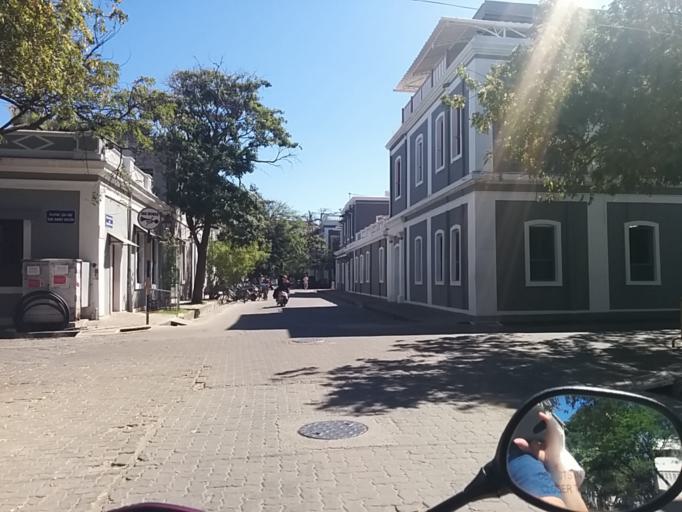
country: IN
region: Pondicherry
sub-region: Puducherry
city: Puducherry
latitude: 11.9371
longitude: 79.8347
